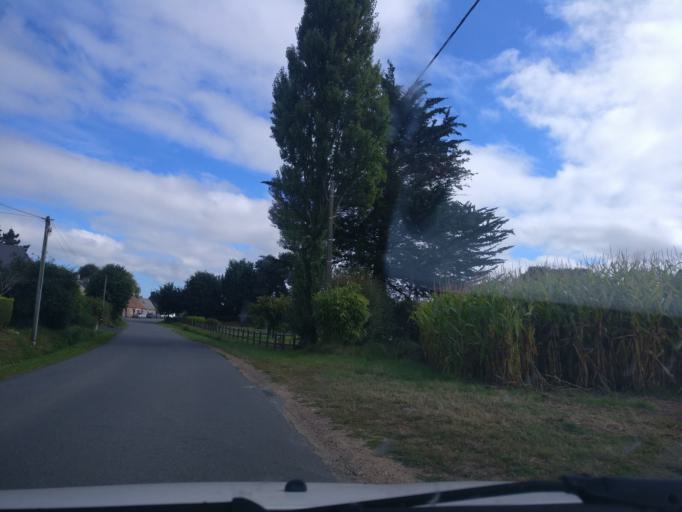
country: FR
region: Brittany
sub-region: Departement des Cotes-d'Armor
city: Rospez
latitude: 48.7331
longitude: -3.3793
